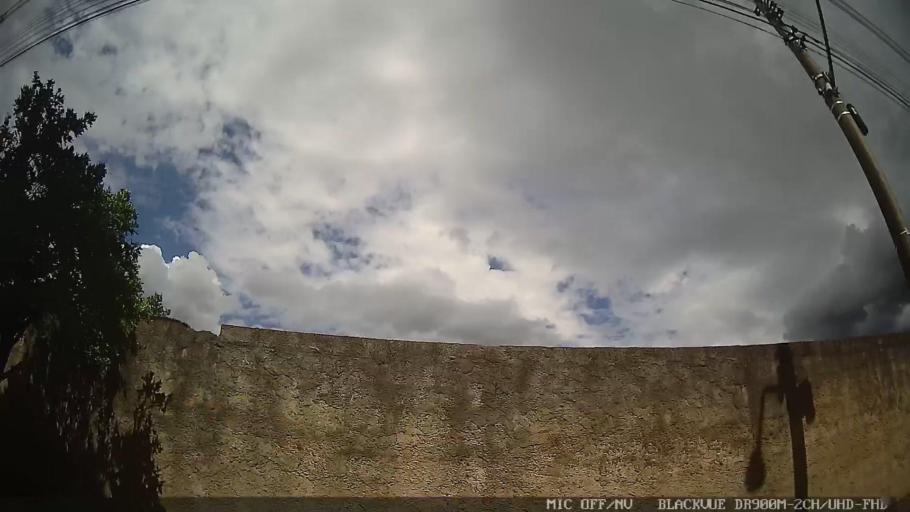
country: BR
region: Sao Paulo
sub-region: Jaguariuna
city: Jaguariuna
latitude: -22.6989
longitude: -46.9811
